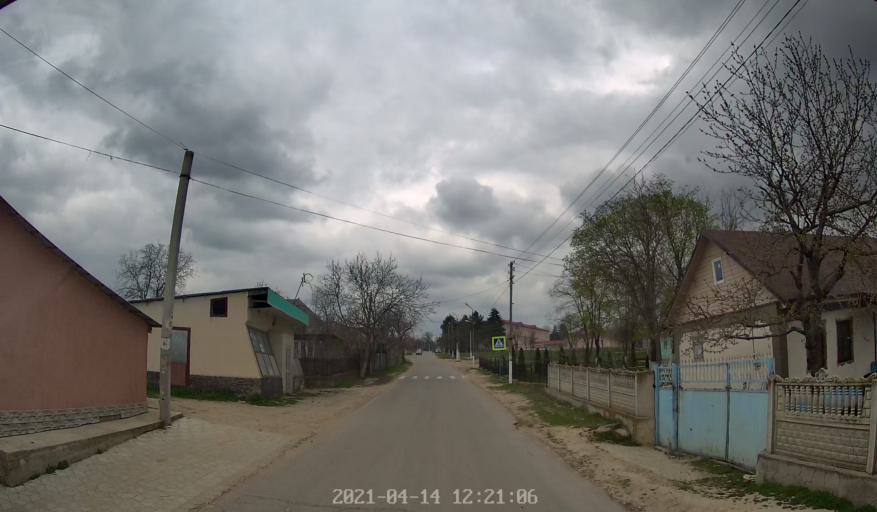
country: MD
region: Criuleni
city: Criuleni
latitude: 47.1680
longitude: 29.1971
